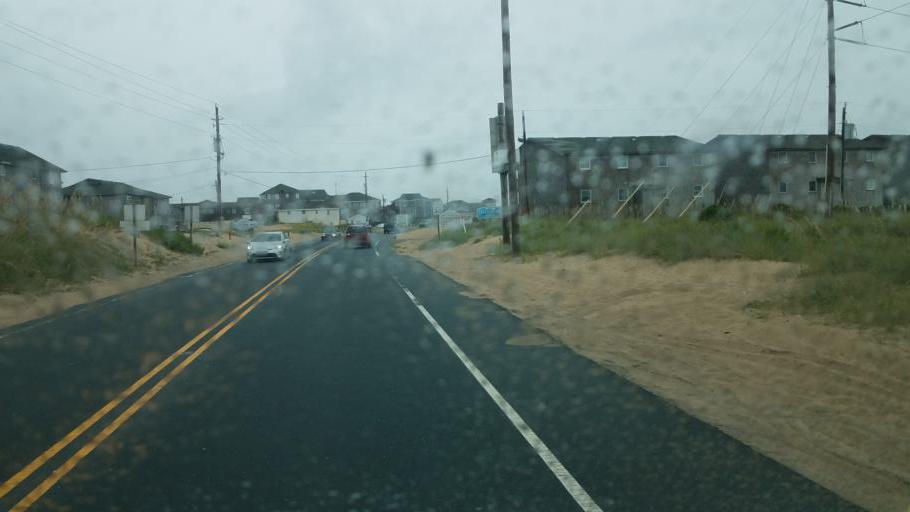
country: US
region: North Carolina
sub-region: Dare County
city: Buxton
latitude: 35.2683
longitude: -75.5189
